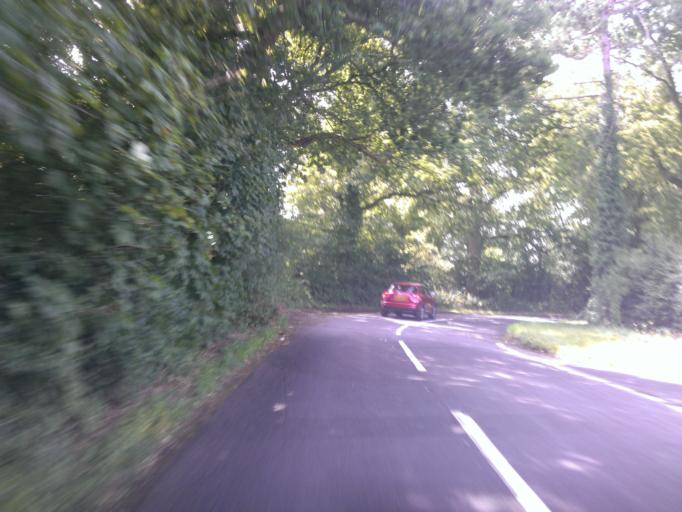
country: GB
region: England
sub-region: Kent
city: Edenbridge
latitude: 51.1962
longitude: 0.1110
